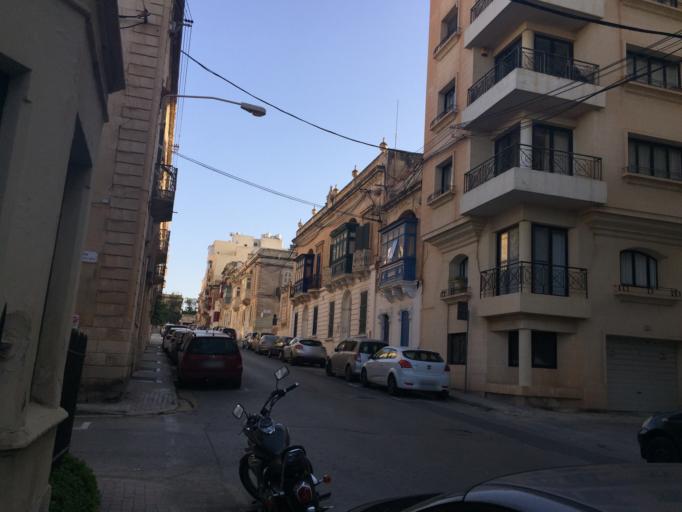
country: MT
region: Tas-Sliema
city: Sliema
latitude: 35.9138
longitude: 14.5029
